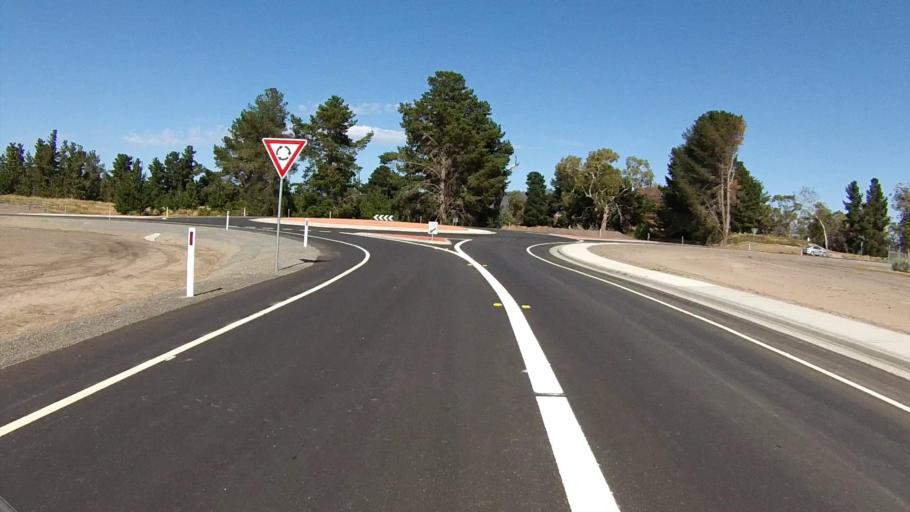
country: AU
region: Tasmania
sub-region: Clarence
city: Seven Mile Beach
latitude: -42.8411
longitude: 147.5031
